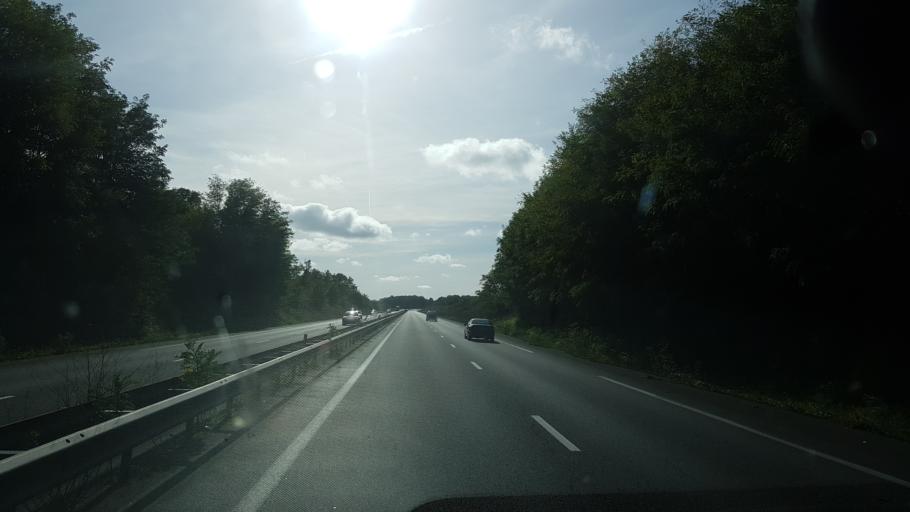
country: FR
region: Poitou-Charentes
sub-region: Departement de la Charente
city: Chasseneuil-sur-Bonnieure
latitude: 45.8014
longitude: 0.4388
